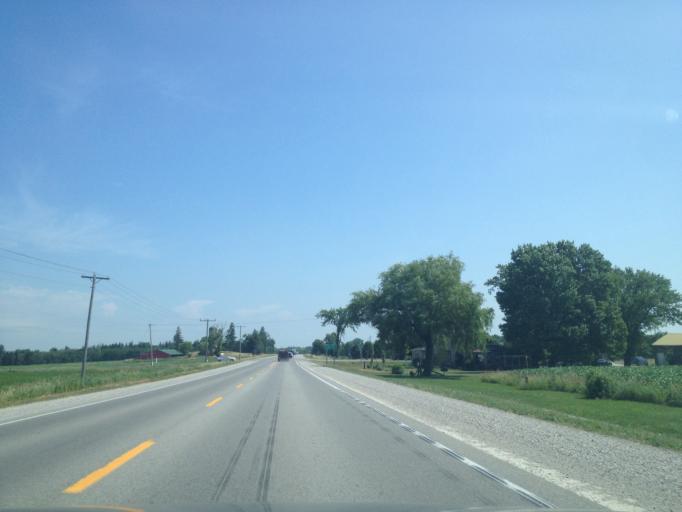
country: CA
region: Ontario
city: Huron East
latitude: 43.4510
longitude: -81.2124
